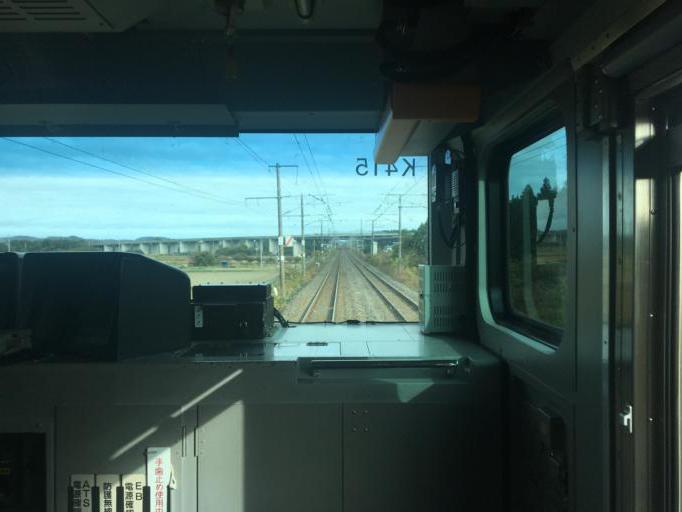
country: JP
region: Ibaraki
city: Tomobe
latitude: 36.3241
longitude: 140.2931
